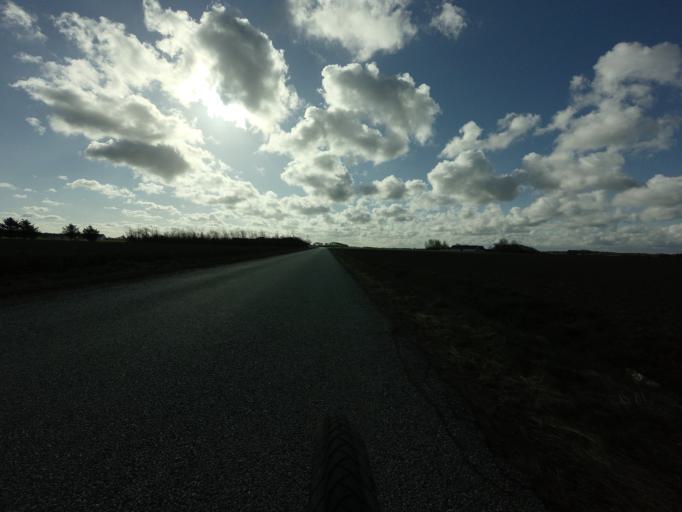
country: DK
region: North Denmark
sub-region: Hjorring Kommune
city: Vra
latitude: 57.3347
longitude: 9.8676
